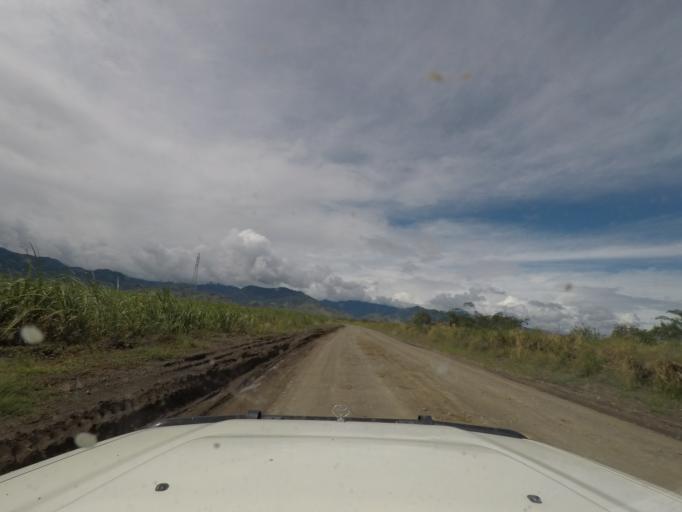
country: PG
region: Eastern Highlands
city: Kainantu
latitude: -6.0284
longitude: 145.9353
